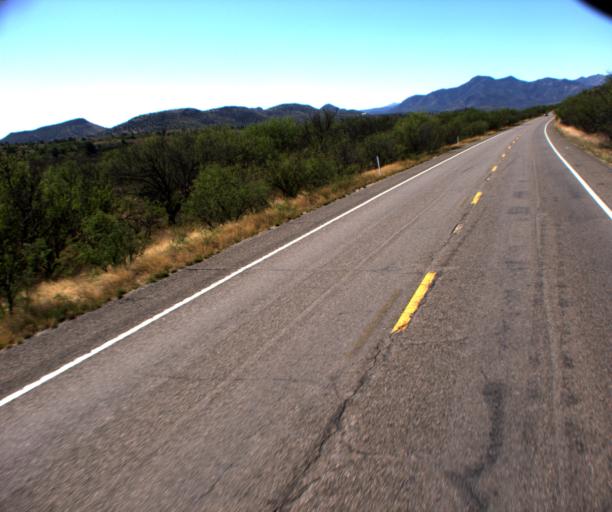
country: US
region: Arizona
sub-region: Santa Cruz County
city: Rio Rico
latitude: 31.6144
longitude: -110.7201
